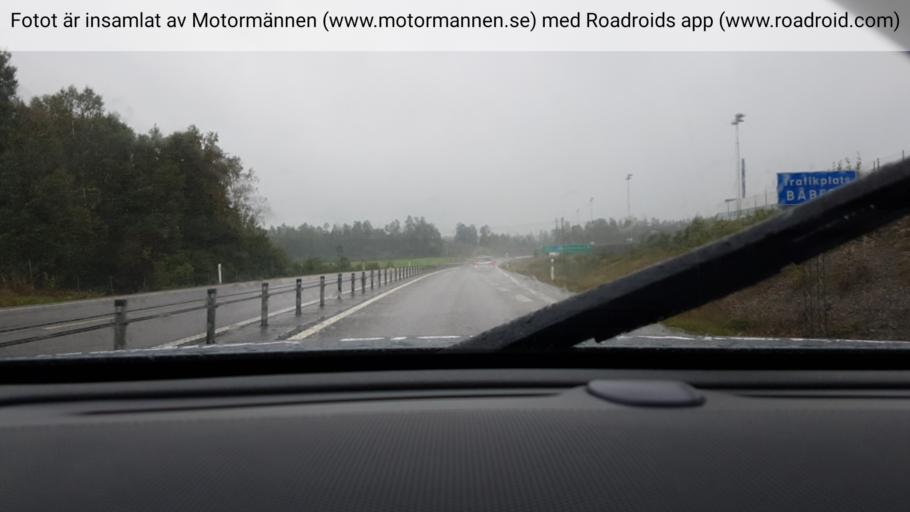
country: SE
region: Vaestra Goetaland
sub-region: Trollhattan
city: Trollhattan
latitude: 58.3443
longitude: 12.2621
